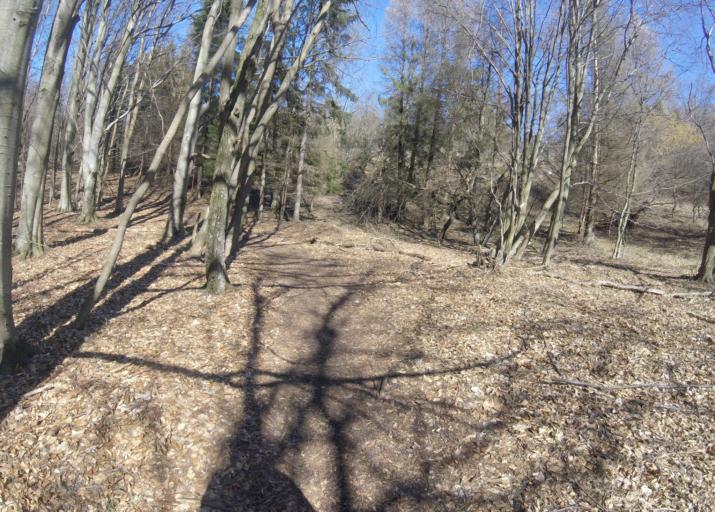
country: HU
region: Heves
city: Szilvasvarad
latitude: 48.0579
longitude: 20.4501
